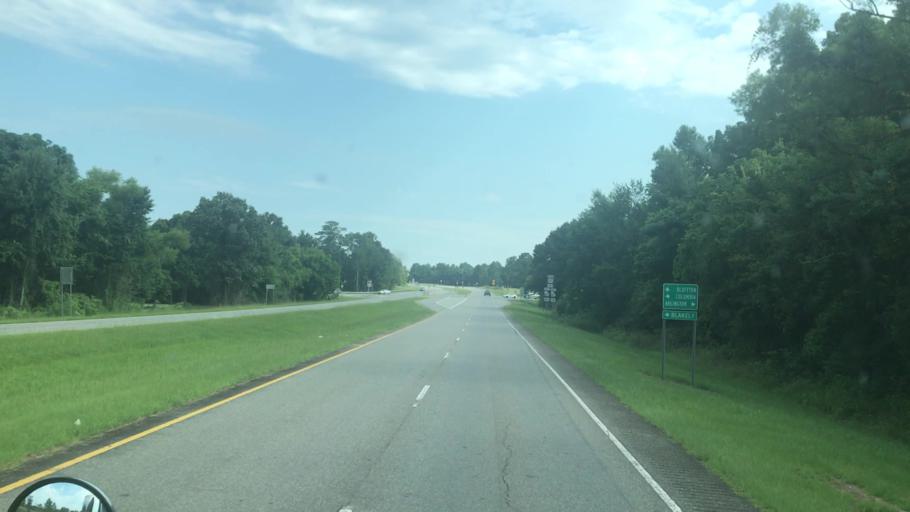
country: US
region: Georgia
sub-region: Early County
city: Blakely
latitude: 31.3784
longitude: -84.9214
